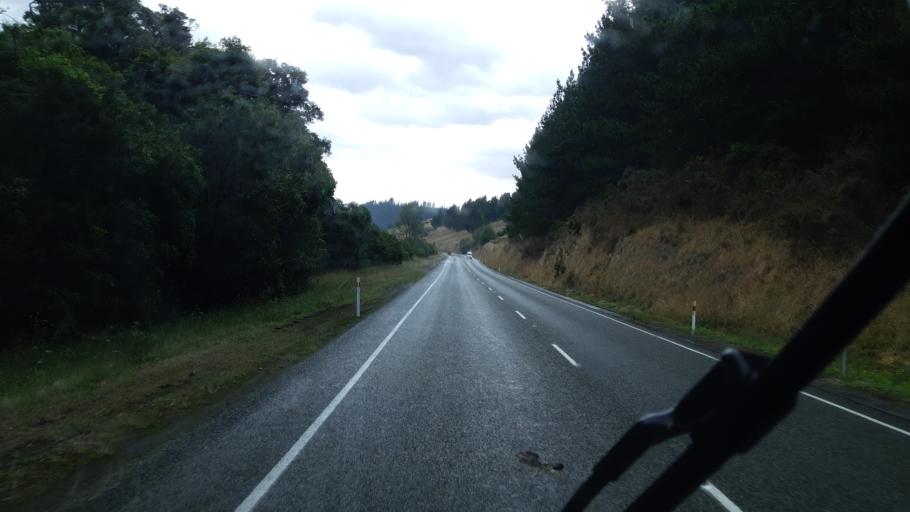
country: NZ
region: Tasman
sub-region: Tasman District
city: Wakefield
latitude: -41.4752
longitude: 172.9346
